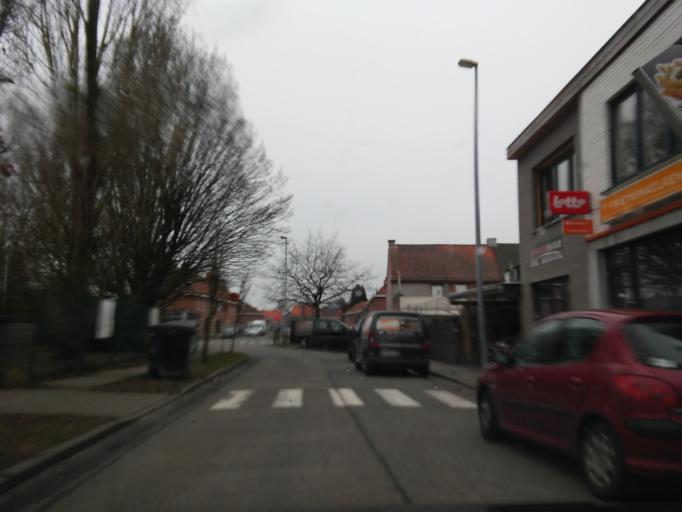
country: BE
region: Flanders
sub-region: Provincie Oost-Vlaanderen
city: Hamme
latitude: 51.0912
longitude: 4.1518
